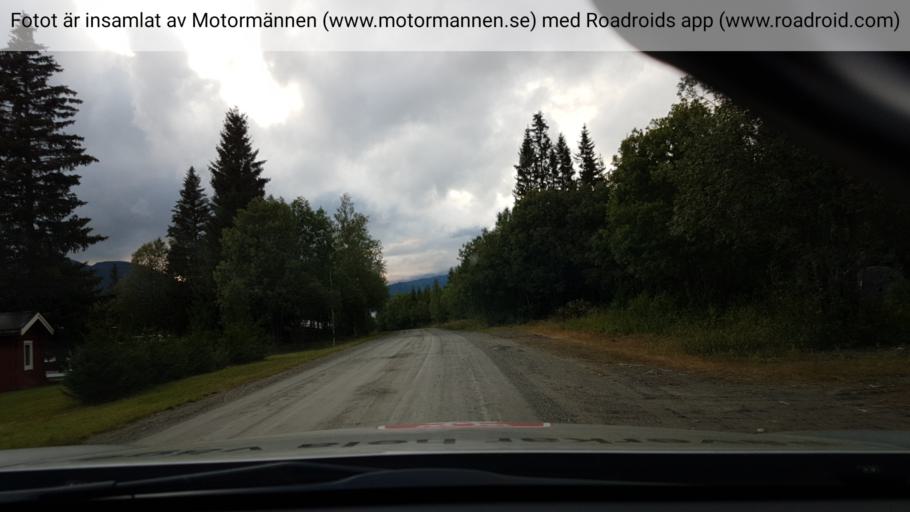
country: SE
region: Vaesterbotten
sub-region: Vilhelmina Kommun
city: Sjoberg
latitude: 65.5094
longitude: 15.6365
